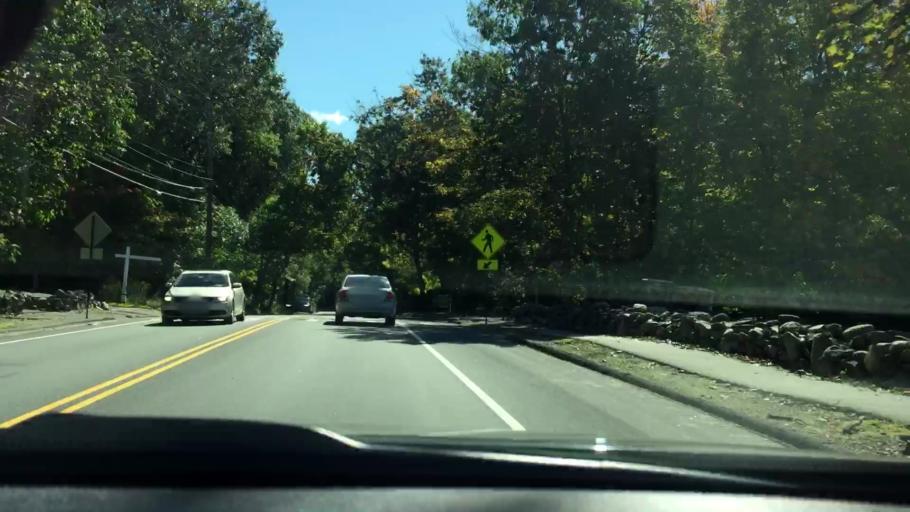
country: US
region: Massachusetts
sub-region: Middlesex County
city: Newton
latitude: 42.3042
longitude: -71.2055
